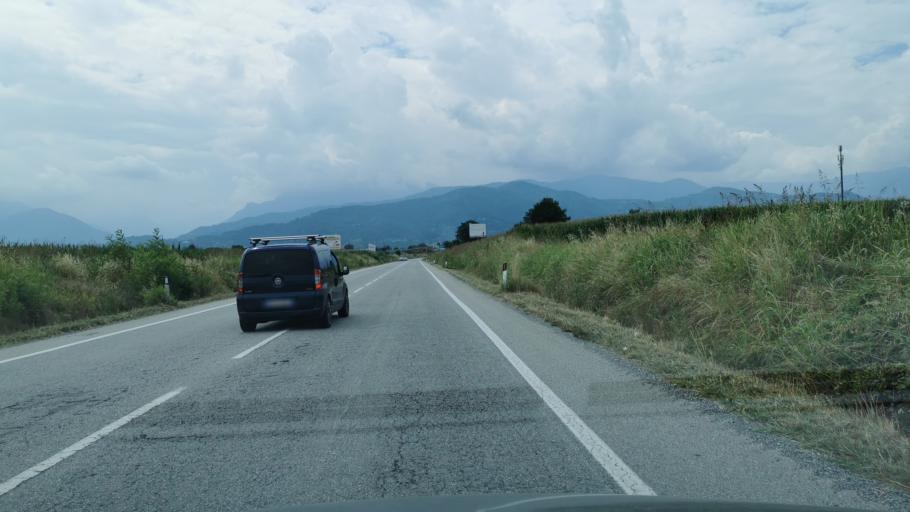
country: IT
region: Piedmont
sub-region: Provincia di Torino
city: Osasco
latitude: 44.8445
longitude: 7.3448
